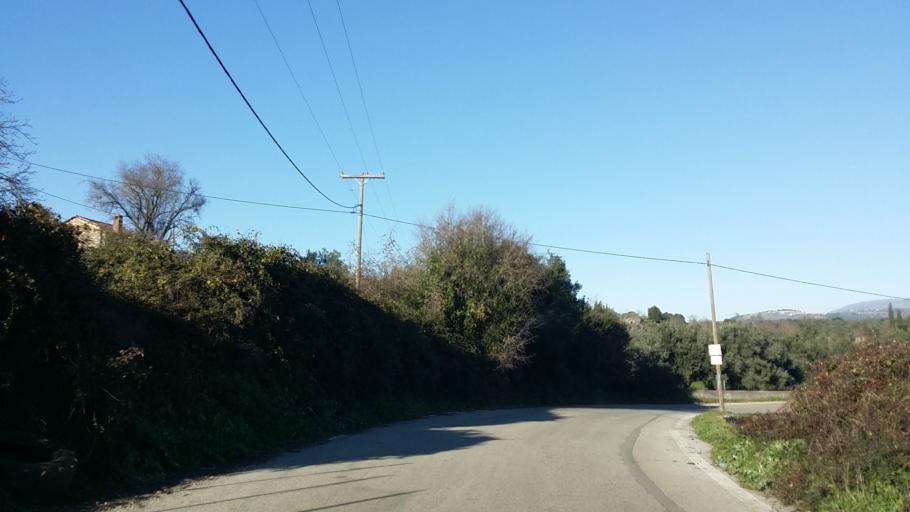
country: GR
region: West Greece
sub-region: Nomos Aitolias kai Akarnanias
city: Fitiai
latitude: 38.6314
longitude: 21.1529
